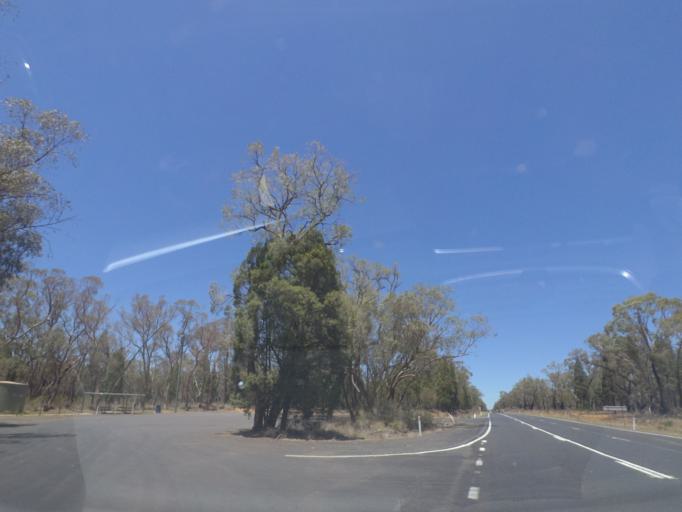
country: AU
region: New South Wales
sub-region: Warrumbungle Shire
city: Coonabarabran
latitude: -30.8539
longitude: 149.4570
